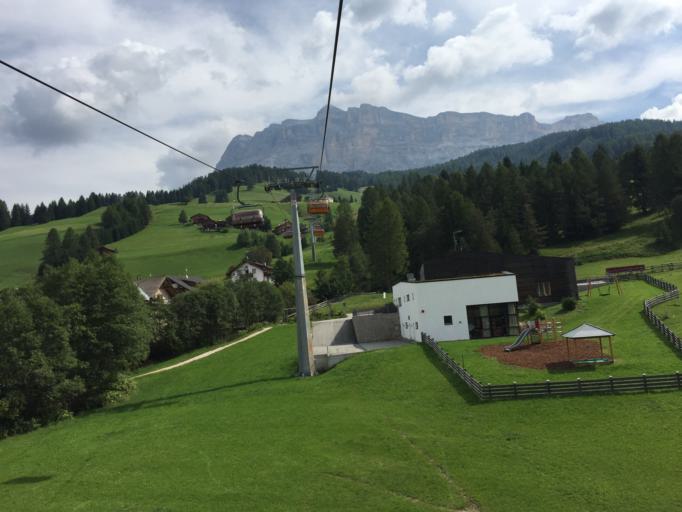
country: IT
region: Trentino-Alto Adige
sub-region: Bolzano
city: Badia
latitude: 46.6097
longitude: 11.8994
